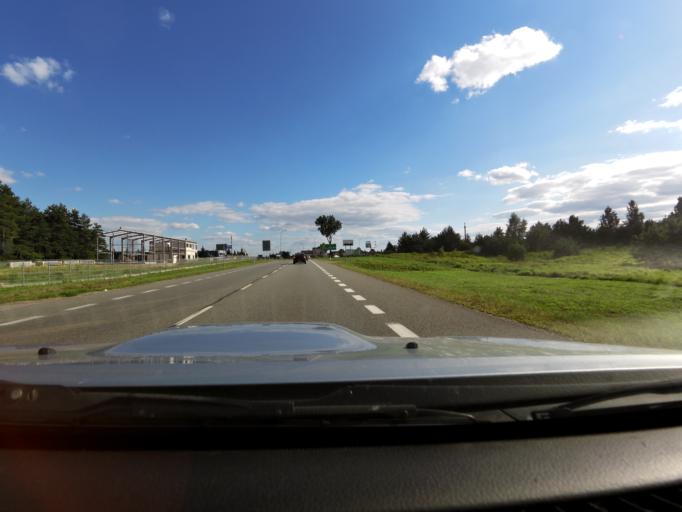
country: PL
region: Warmian-Masurian Voivodeship
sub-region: Powiat elcki
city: Elk
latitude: 53.8353
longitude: 22.3894
